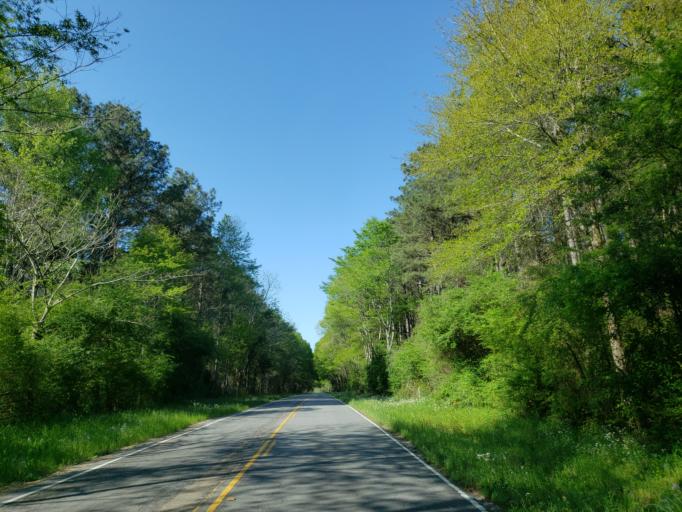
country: US
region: Mississippi
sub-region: Forrest County
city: Rawls Springs
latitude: 31.5091
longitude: -89.3601
